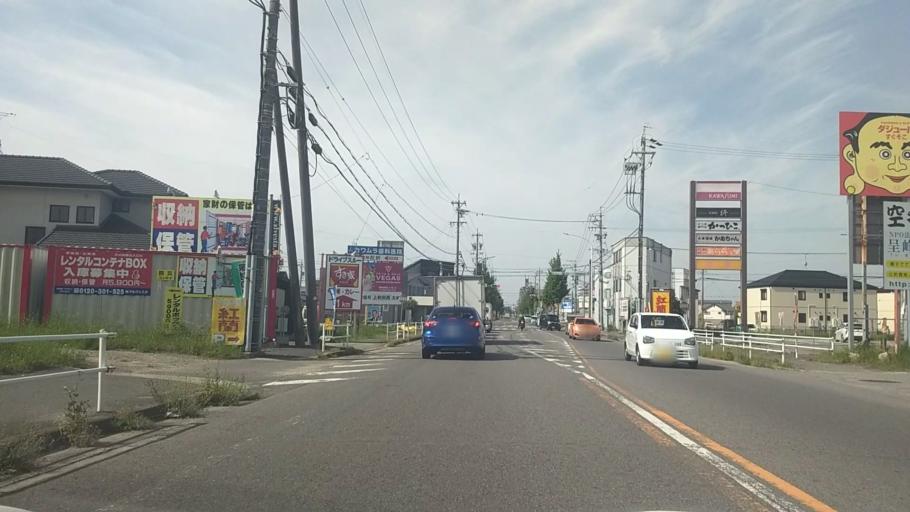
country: JP
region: Aichi
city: Okazaki
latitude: 34.9387
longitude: 137.1492
